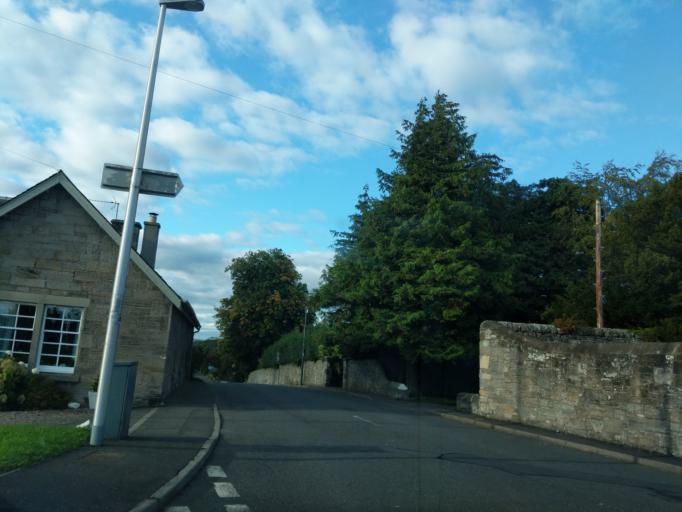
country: GB
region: Scotland
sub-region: Edinburgh
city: Queensferry
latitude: 55.9824
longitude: -3.3735
